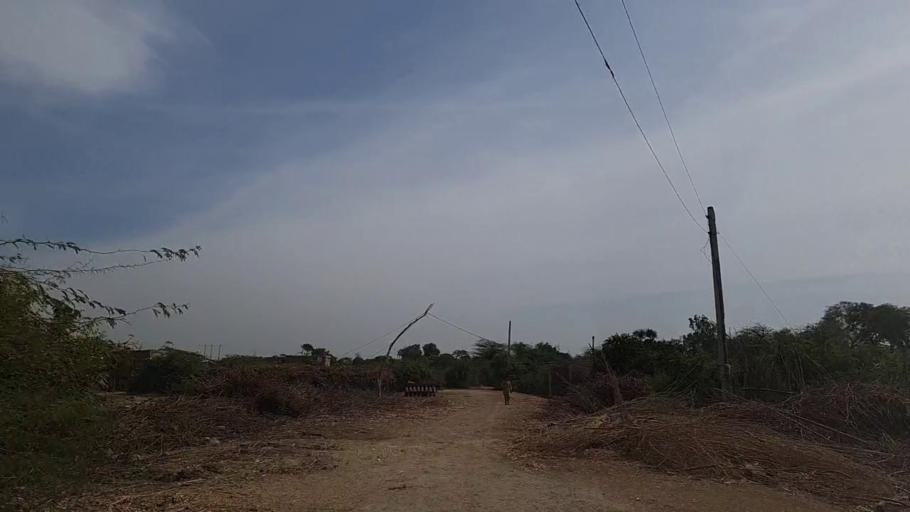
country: PK
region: Sindh
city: Samaro
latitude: 25.2908
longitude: 69.4170
